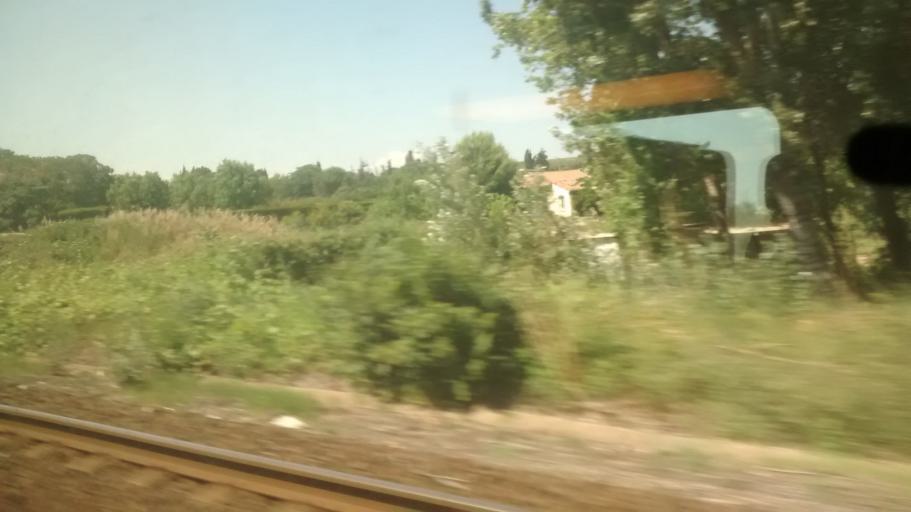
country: FR
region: Languedoc-Roussillon
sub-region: Departement de l'Herault
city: Lunel
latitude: 43.6798
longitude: 4.1185
